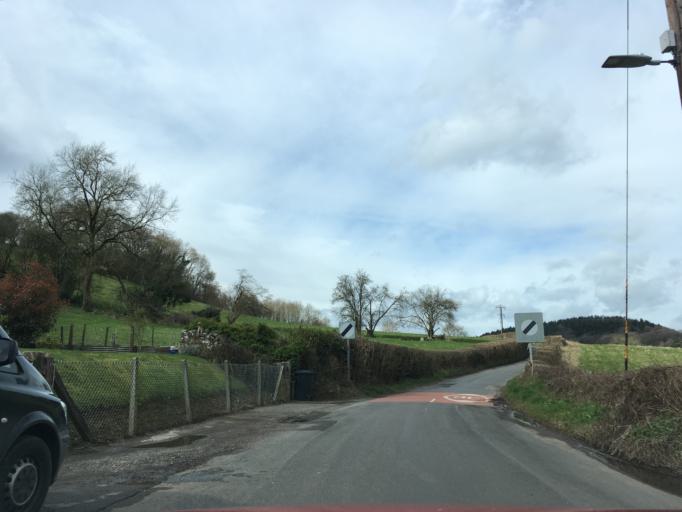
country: GB
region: England
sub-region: Gloucestershire
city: Coleford
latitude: 51.7735
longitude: -2.6313
